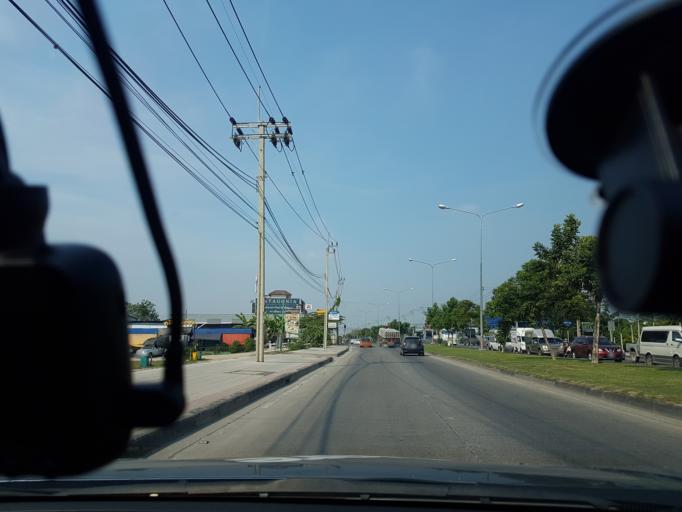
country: TH
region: Bangkok
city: Khlong Sam Wa
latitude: 13.8631
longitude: 100.7225
